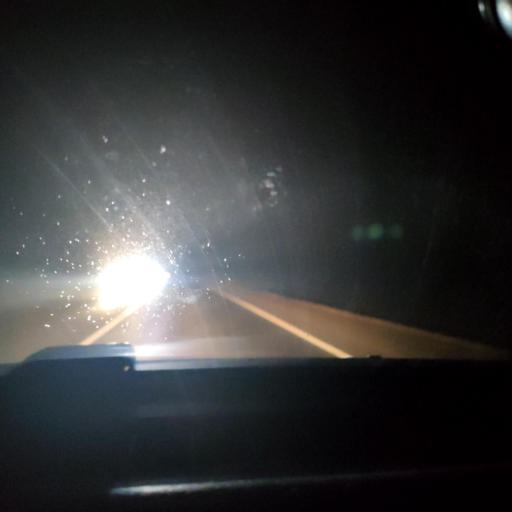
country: RU
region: Voronezj
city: Latnaya
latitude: 51.6400
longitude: 38.6885
